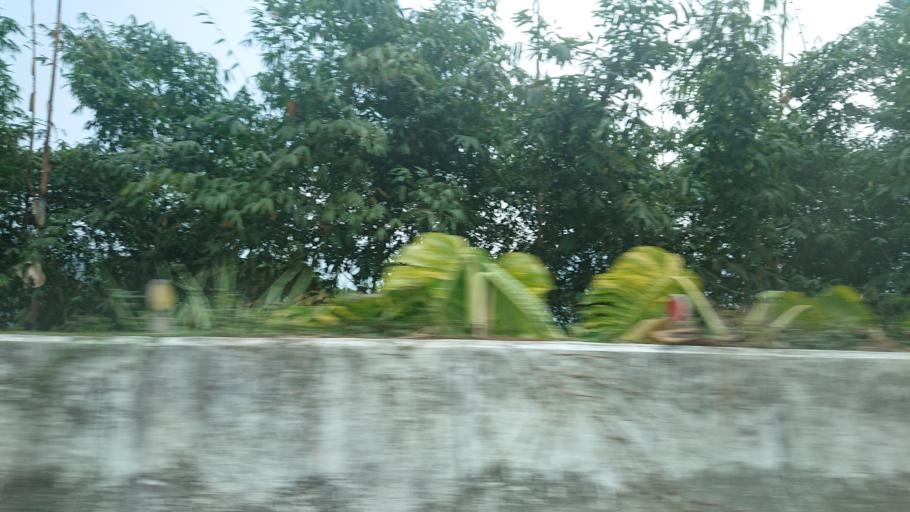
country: TW
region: Taiwan
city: Lugu
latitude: 23.5838
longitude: 120.6965
